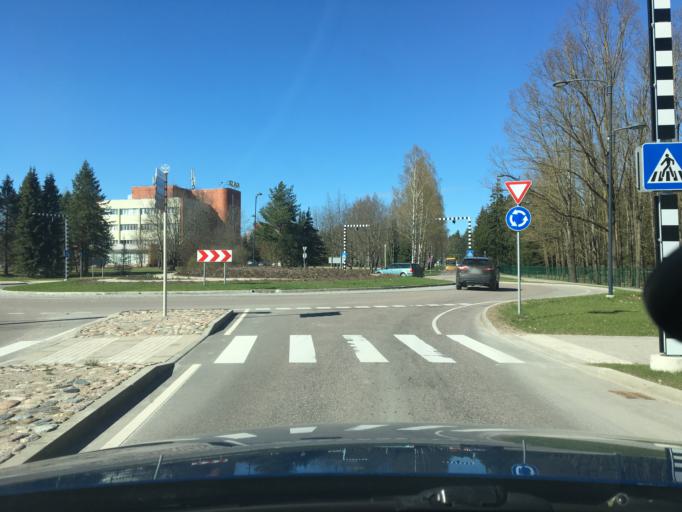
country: LV
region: Salaspils
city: Salaspils
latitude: 56.8683
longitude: 24.3523
